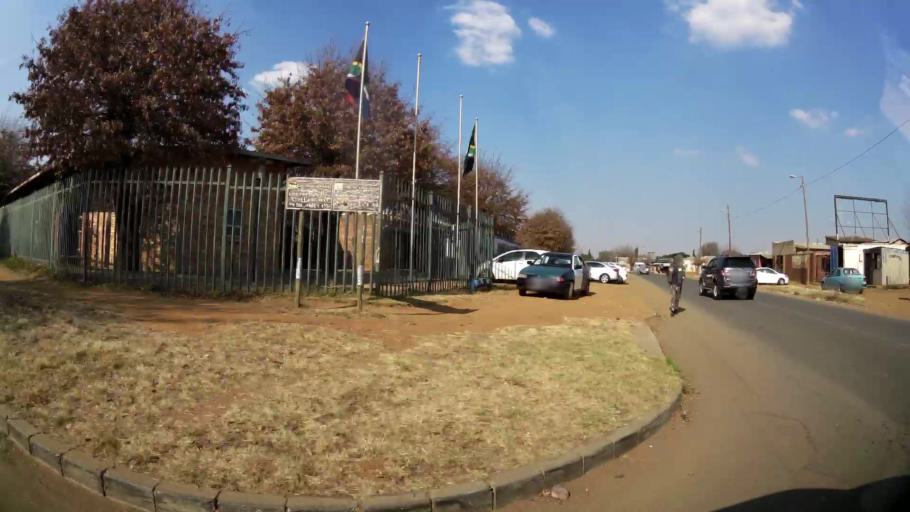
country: ZA
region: Gauteng
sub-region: Ekurhuleni Metropolitan Municipality
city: Brakpan
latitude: -26.1532
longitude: 28.4145
